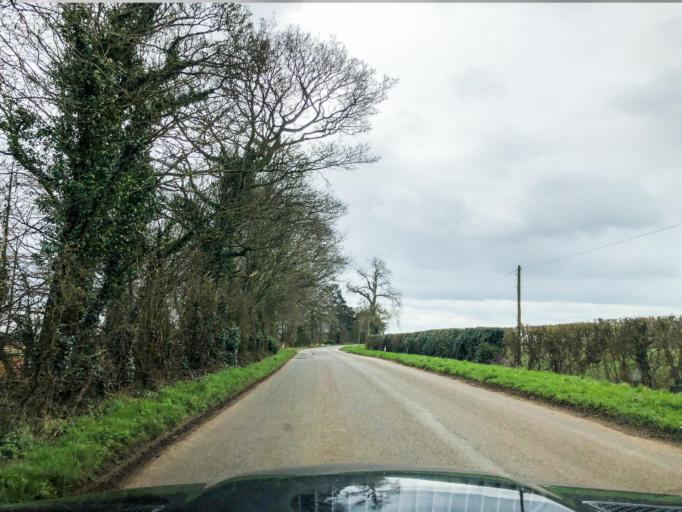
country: GB
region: England
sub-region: Oxfordshire
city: Hanwell
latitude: 52.1054
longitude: -1.4751
